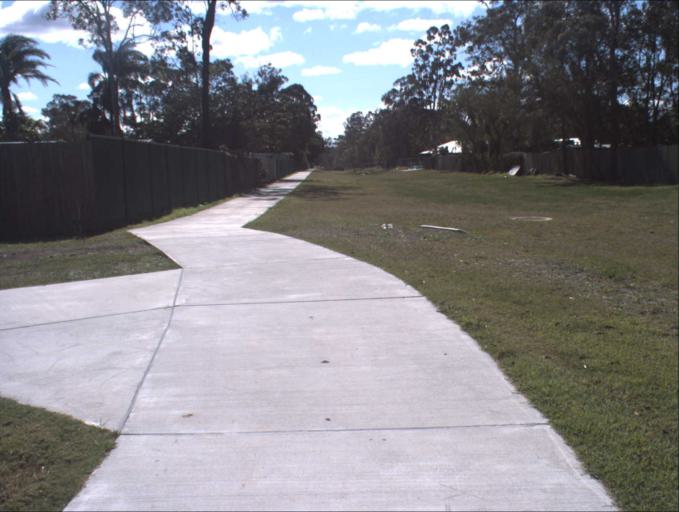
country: AU
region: Queensland
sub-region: Logan
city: Waterford West
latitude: -27.6769
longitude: 153.1082
